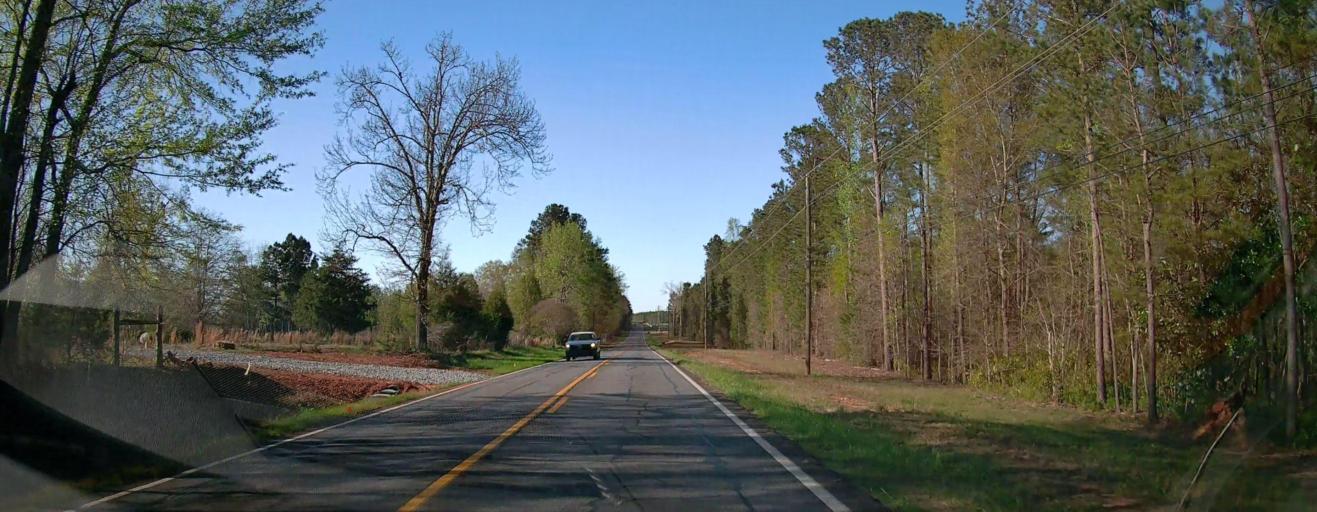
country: US
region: Georgia
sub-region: Butts County
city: Indian Springs
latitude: 33.1571
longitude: -83.9564
